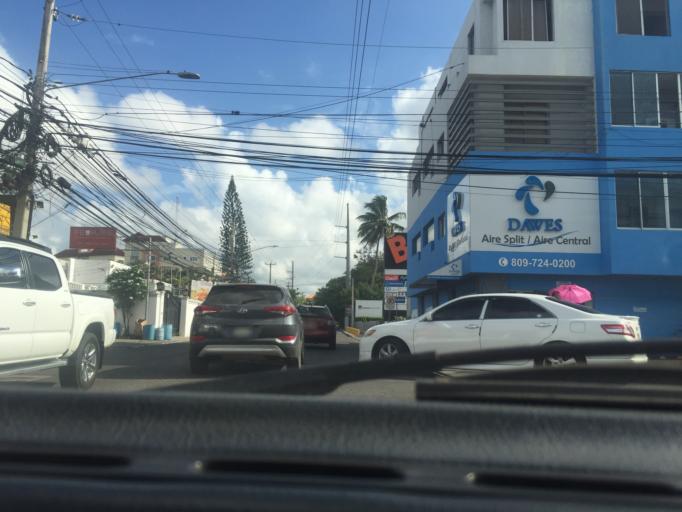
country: DO
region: Santiago
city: Santiago de los Caballeros
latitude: 19.4546
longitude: -70.6656
